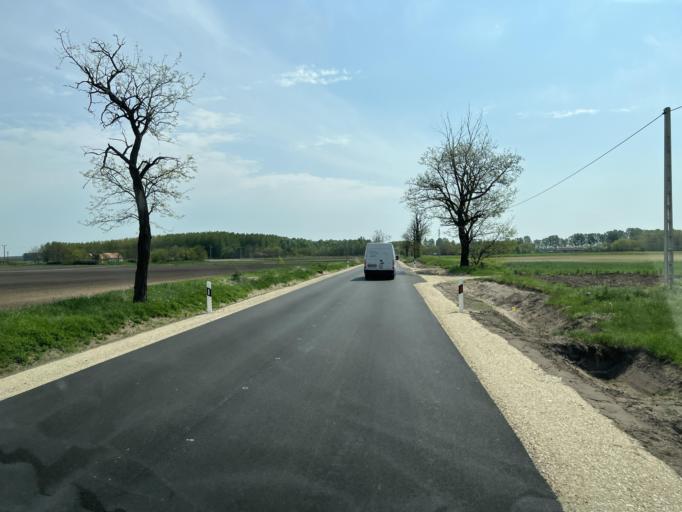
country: HU
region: Pest
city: Nagykoros
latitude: 47.0215
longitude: 19.8414
